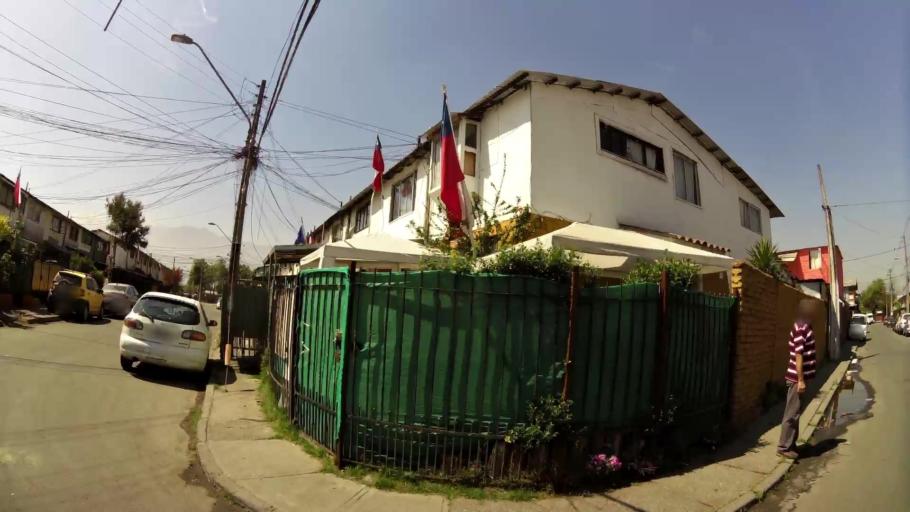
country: CL
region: Santiago Metropolitan
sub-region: Provincia de Santiago
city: La Pintana
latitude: -33.5569
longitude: -70.6035
